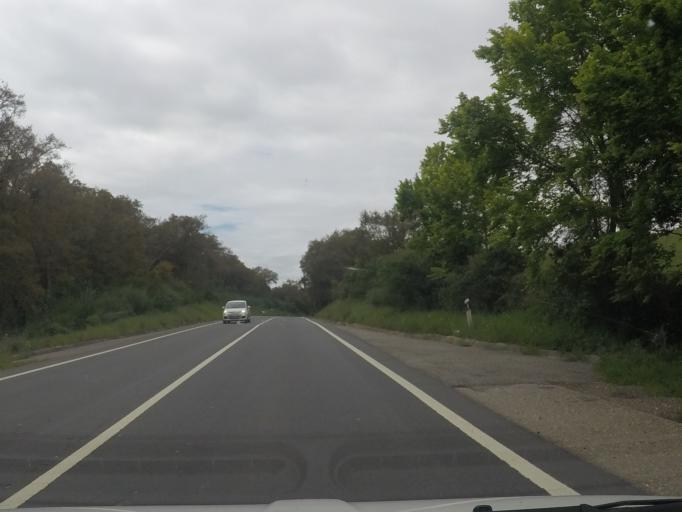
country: PT
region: Setubal
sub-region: Santiago do Cacem
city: Cercal
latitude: 37.8319
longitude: -8.7017
